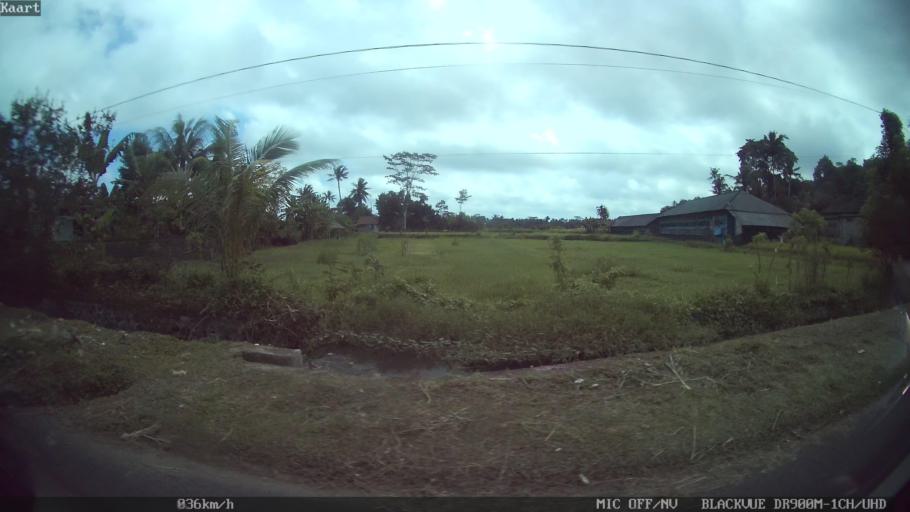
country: ID
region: Bali
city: Banjar Abuan
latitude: -8.4564
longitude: 115.3406
